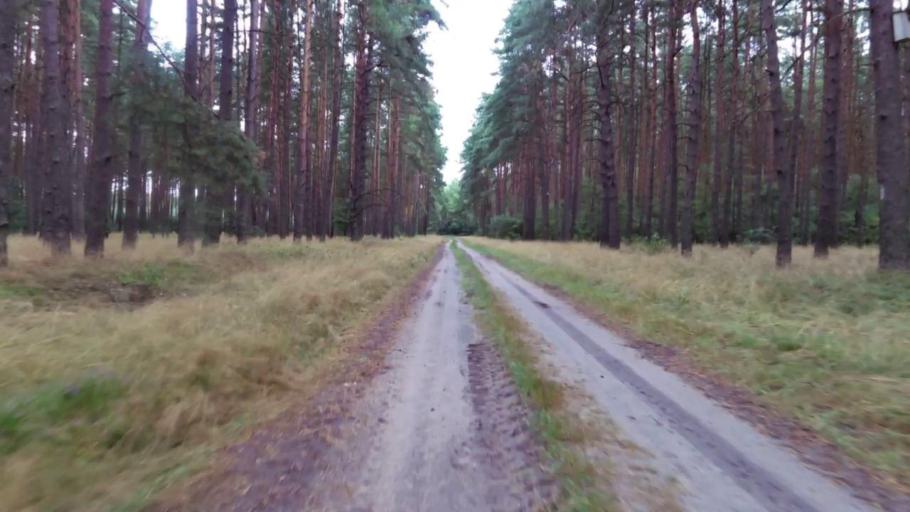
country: PL
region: West Pomeranian Voivodeship
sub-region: Powiat mysliborski
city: Debno
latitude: 52.8253
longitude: 14.6760
